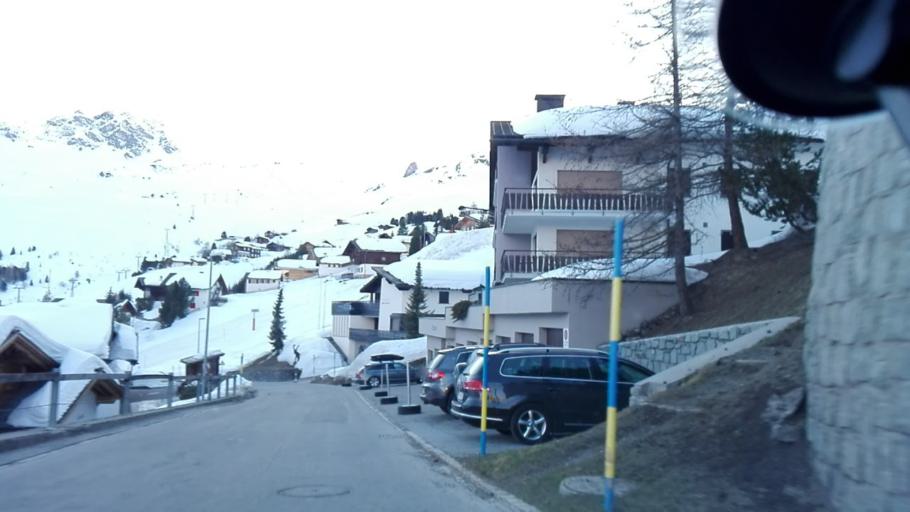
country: CH
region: Grisons
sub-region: Plessur District
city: Arosa
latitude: 46.7744
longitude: 9.6606
